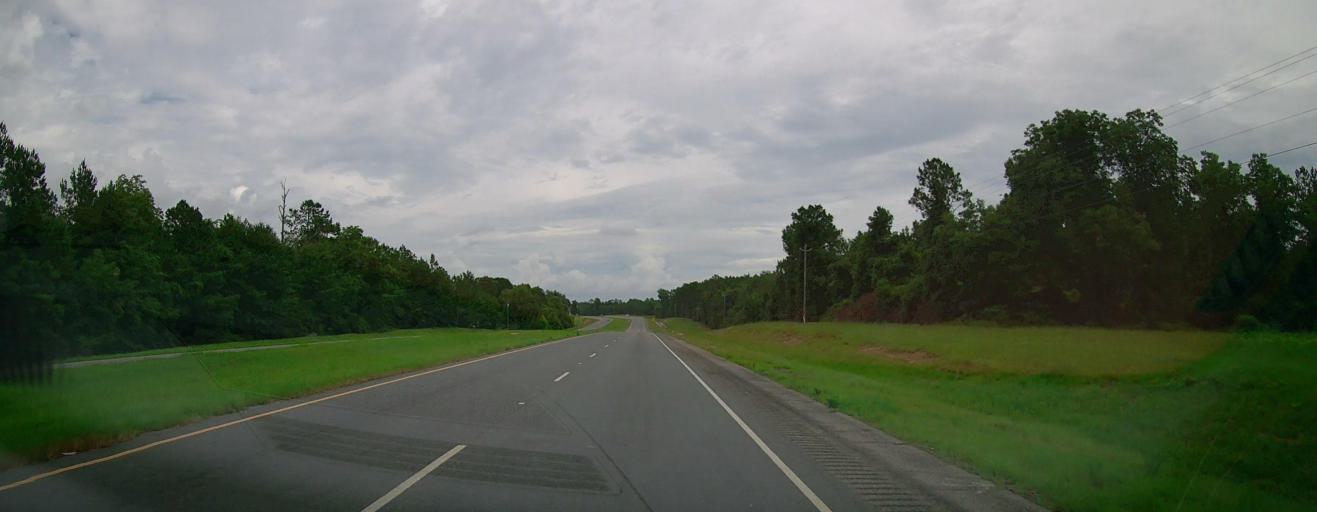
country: US
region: Georgia
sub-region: Telfair County
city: Helena
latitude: 32.1029
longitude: -83.0204
